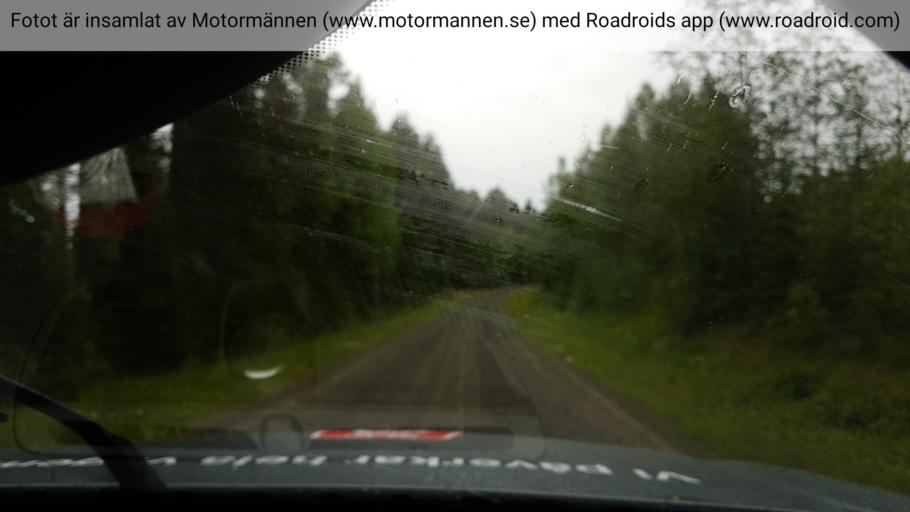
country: SE
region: Jaemtland
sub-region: Bergs Kommun
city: Hoverberg
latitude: 62.5251
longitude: 14.7114
